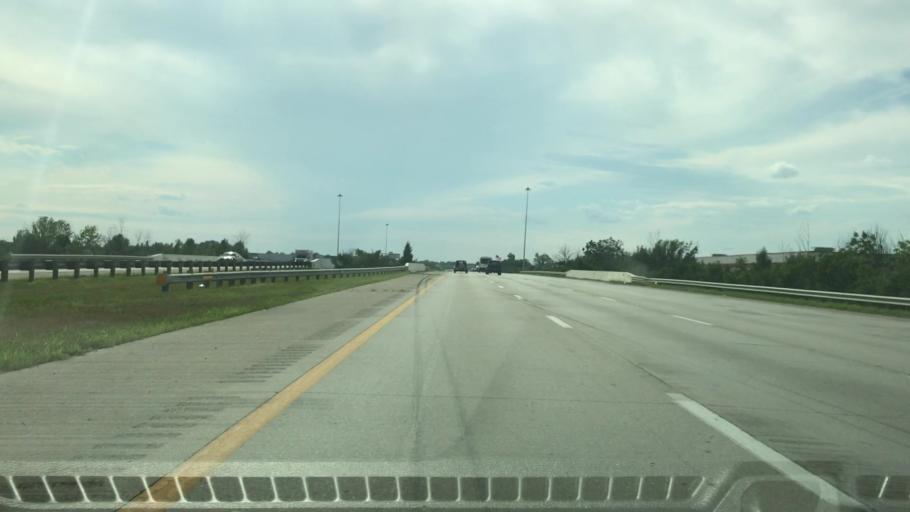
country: US
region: Ohio
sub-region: Franklin County
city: Grove City
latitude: 39.9042
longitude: -83.0770
